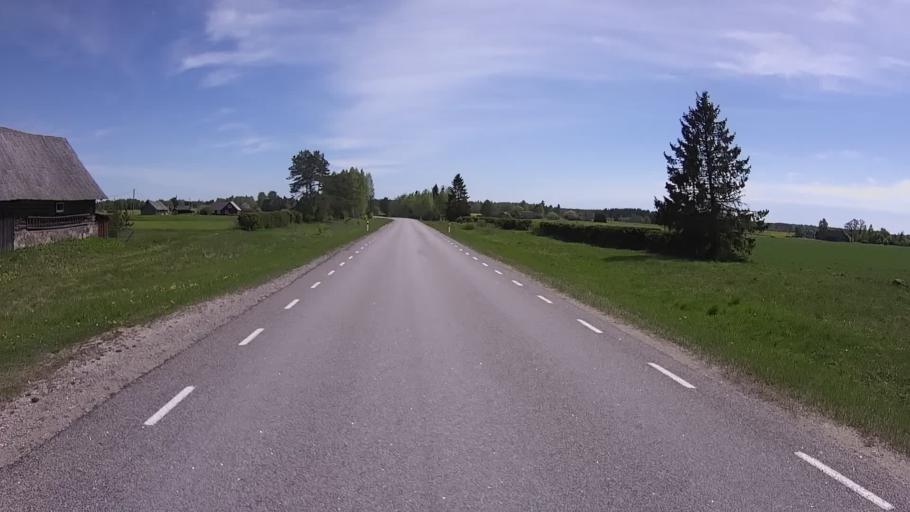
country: EE
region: Vorumaa
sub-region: Antsla vald
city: Vana-Antsla
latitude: 57.6158
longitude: 26.3599
